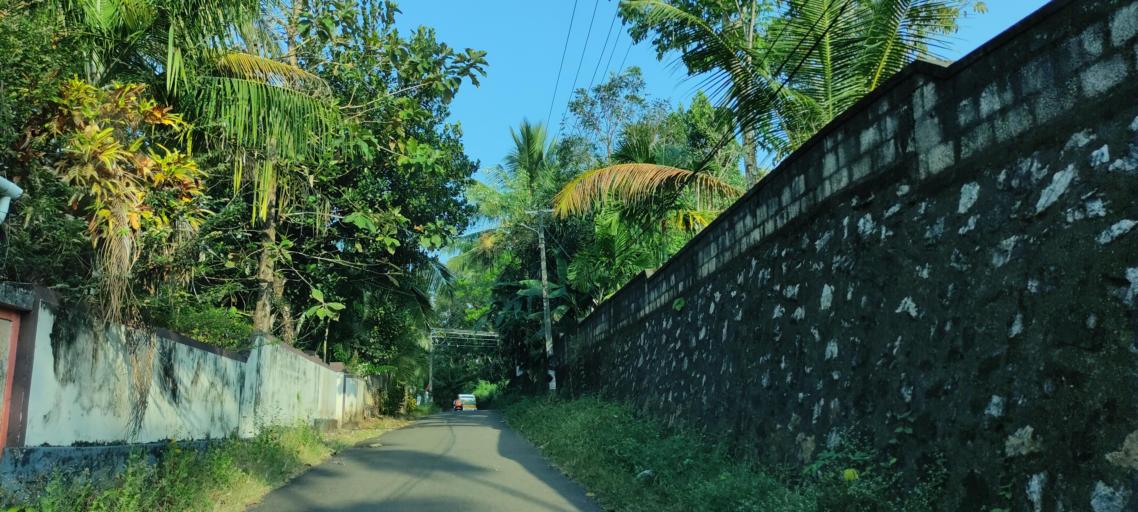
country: IN
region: Kerala
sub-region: Pattanamtitta
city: Adur
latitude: 9.1505
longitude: 76.7591
